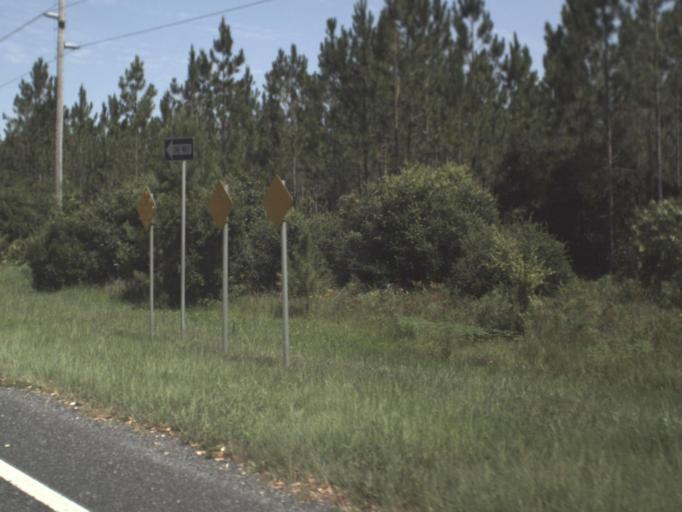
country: US
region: Florida
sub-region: Dixie County
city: Cross City
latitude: 29.6499
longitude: -83.1633
